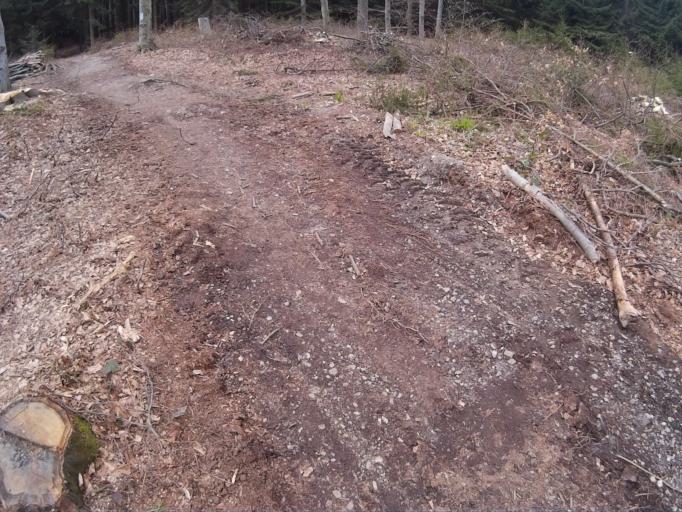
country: AT
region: Burgenland
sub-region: Politischer Bezirk Oberwart
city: Rechnitz
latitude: 47.3529
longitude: 16.4365
